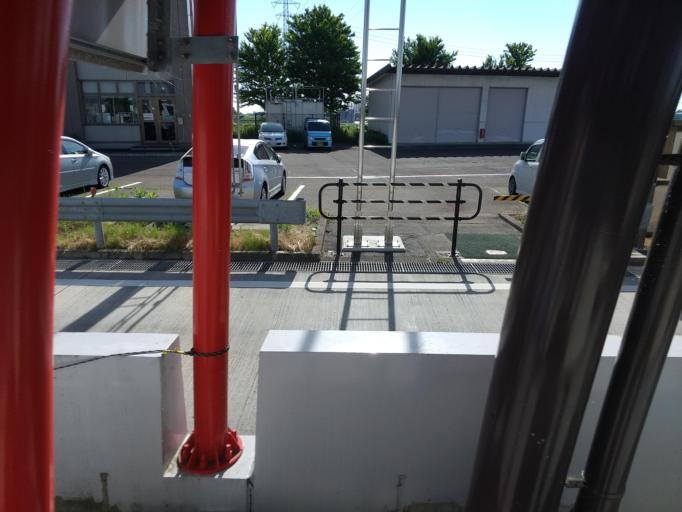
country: JP
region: Miyagi
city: Sendai
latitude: 38.2153
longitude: 140.9047
